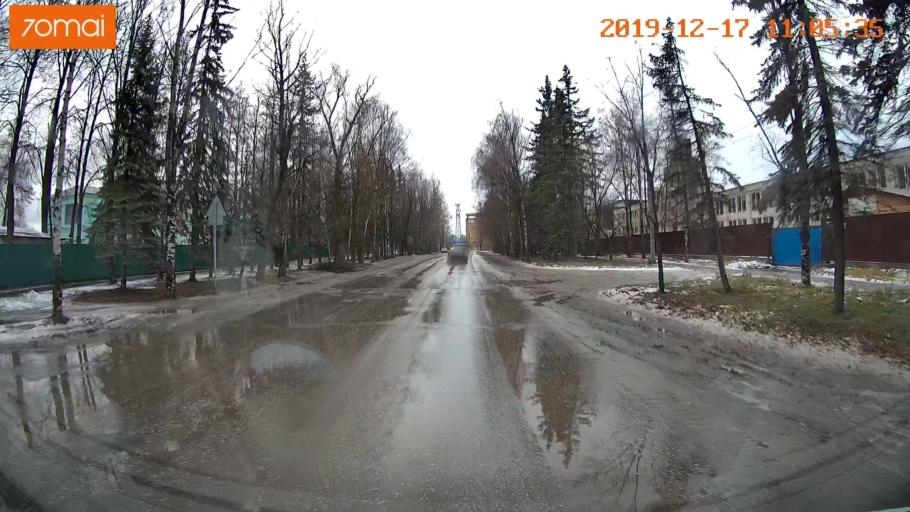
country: RU
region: Vladimir
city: Gus'-Khrustal'nyy
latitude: 55.6202
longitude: 40.6430
